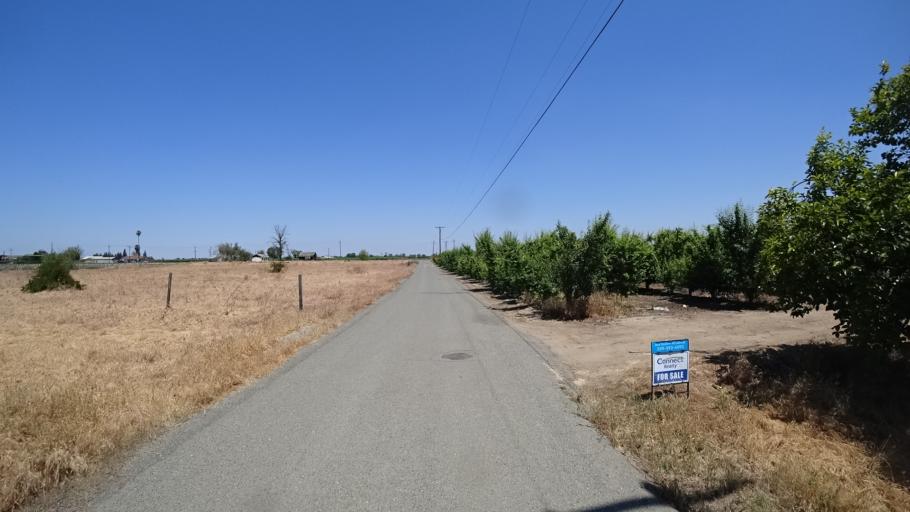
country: US
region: California
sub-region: Fresno County
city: Kingsburg
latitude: 36.4870
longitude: -119.5460
